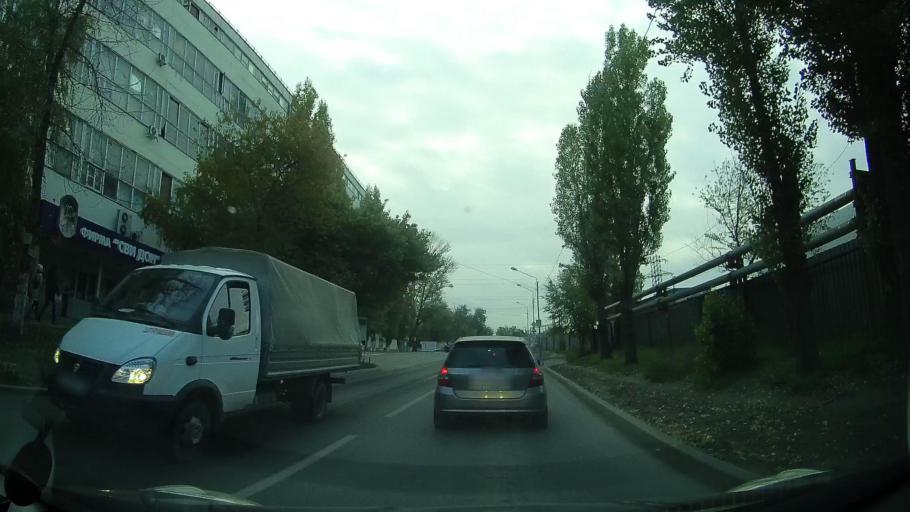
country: RU
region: Rostov
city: Rostov-na-Donu
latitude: 47.2428
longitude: 39.6697
